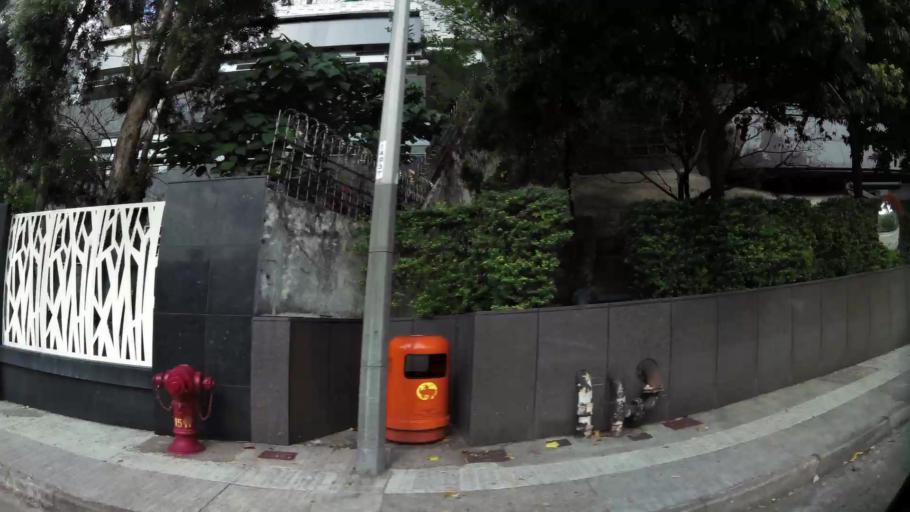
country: HK
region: Wanchai
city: Wan Chai
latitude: 22.2711
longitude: 114.1866
